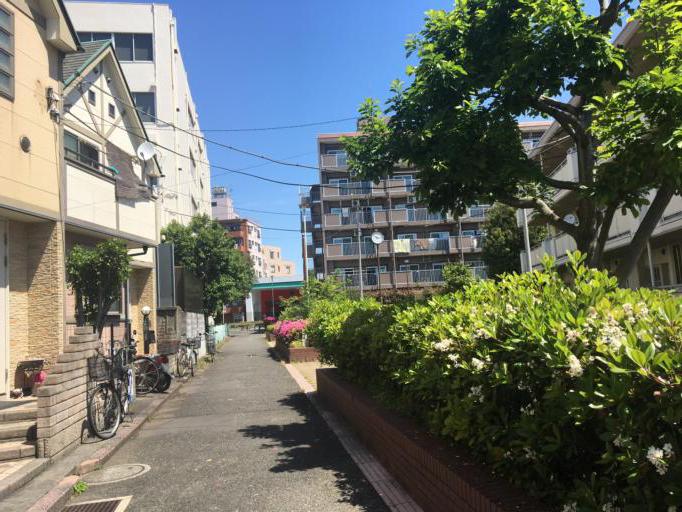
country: JP
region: Saitama
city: Wako
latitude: 35.7622
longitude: 139.6681
